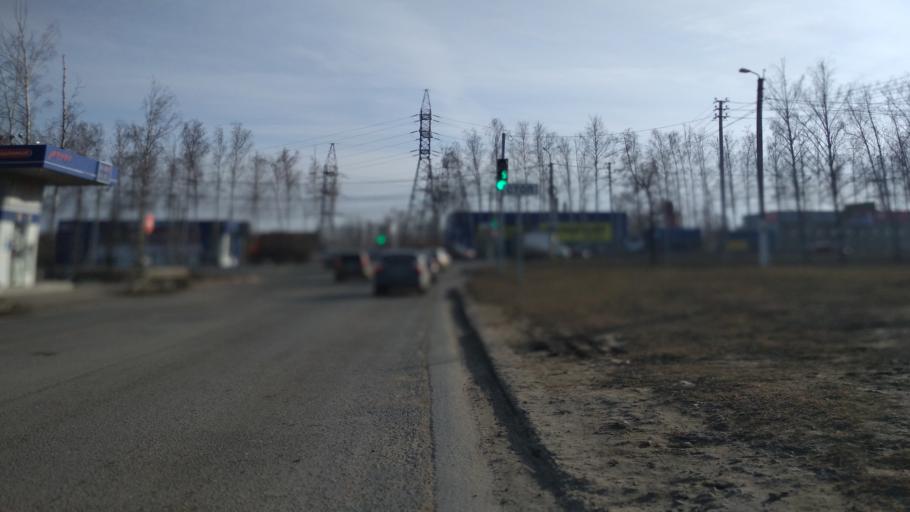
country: RU
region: Chuvashia
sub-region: Cheboksarskiy Rayon
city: Cheboksary
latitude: 56.1287
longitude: 47.3165
